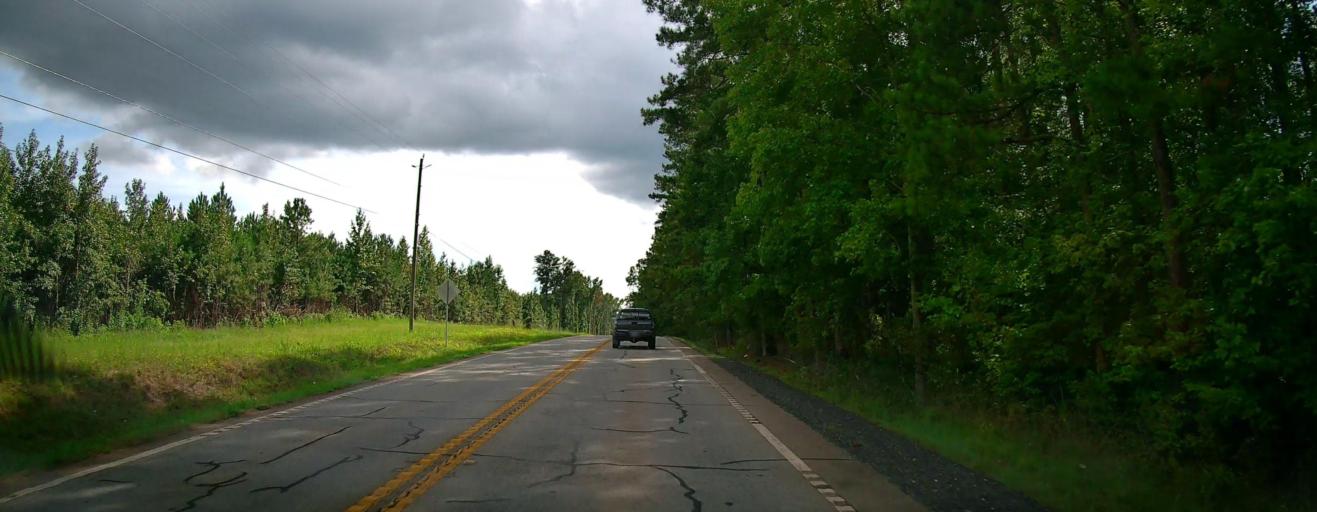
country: US
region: Georgia
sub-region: Harris County
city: Hamilton
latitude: 32.7361
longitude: -84.8715
